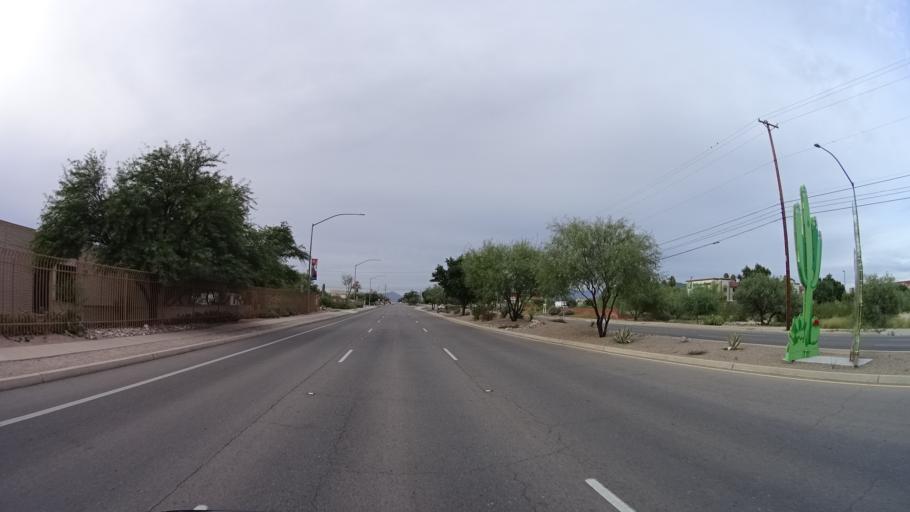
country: US
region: Arizona
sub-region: Pima County
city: Summit
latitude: 32.1291
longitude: -110.9347
